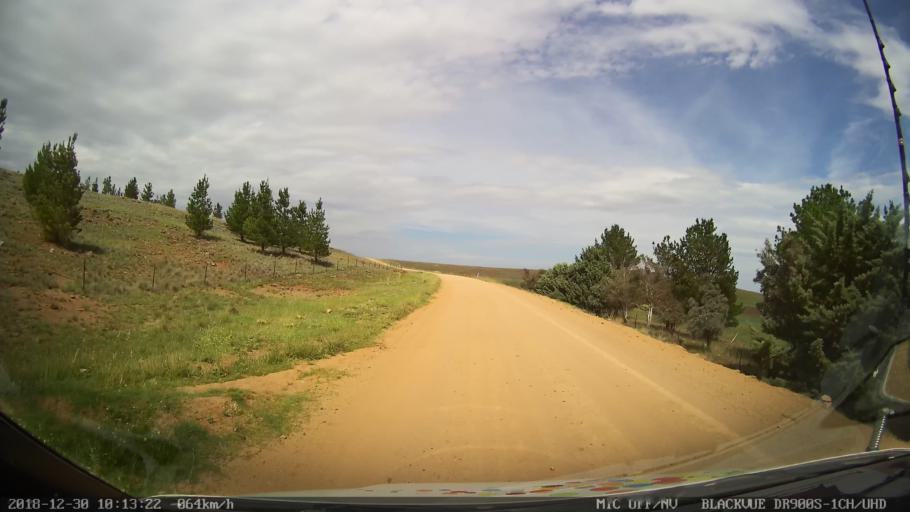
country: AU
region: New South Wales
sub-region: Snowy River
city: Berridale
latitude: -36.5381
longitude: 149.0661
